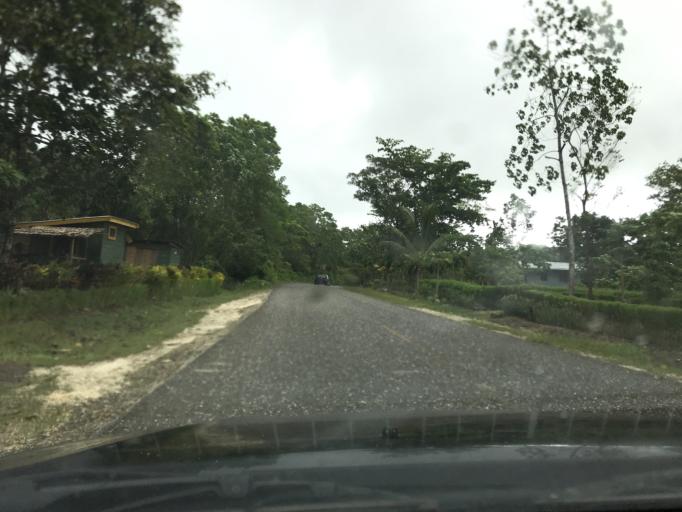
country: SB
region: Western Province
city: Gizo
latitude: -8.3193
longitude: 157.2556
